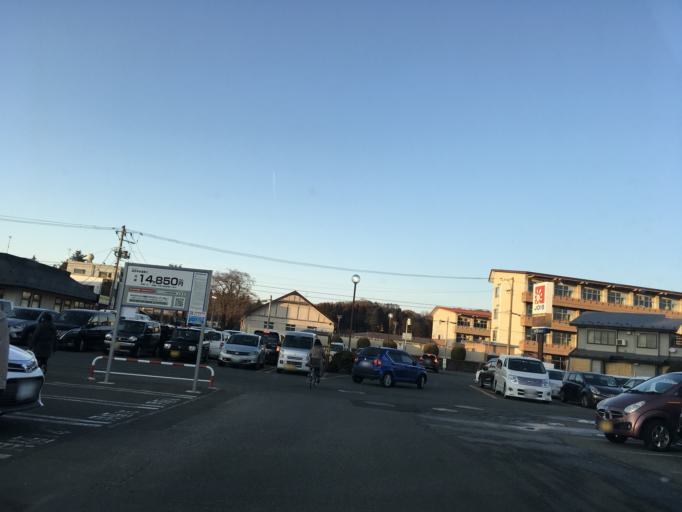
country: JP
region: Iwate
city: Morioka-shi
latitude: 39.7073
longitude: 141.1551
